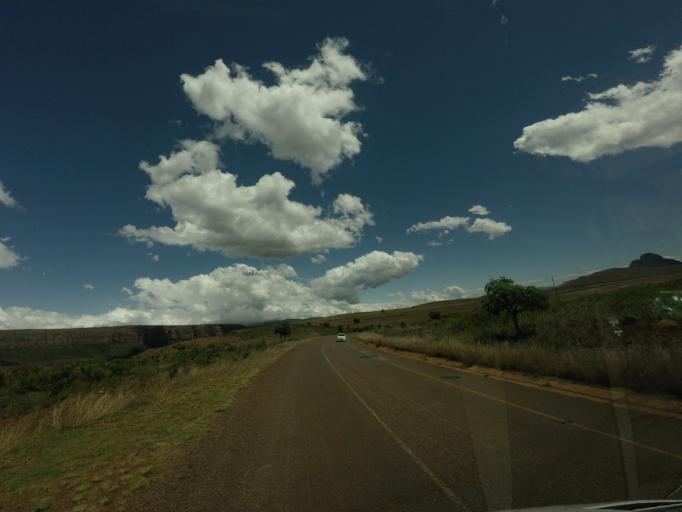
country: ZA
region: Limpopo
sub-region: Mopani District Municipality
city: Hoedspruit
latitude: -24.6089
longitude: 30.8149
